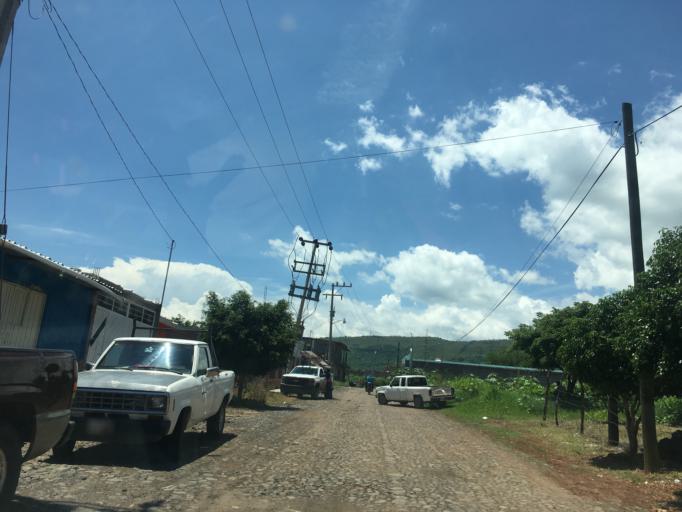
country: MX
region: Nayarit
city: Ixtlan del Rio
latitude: 21.0366
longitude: -104.3538
